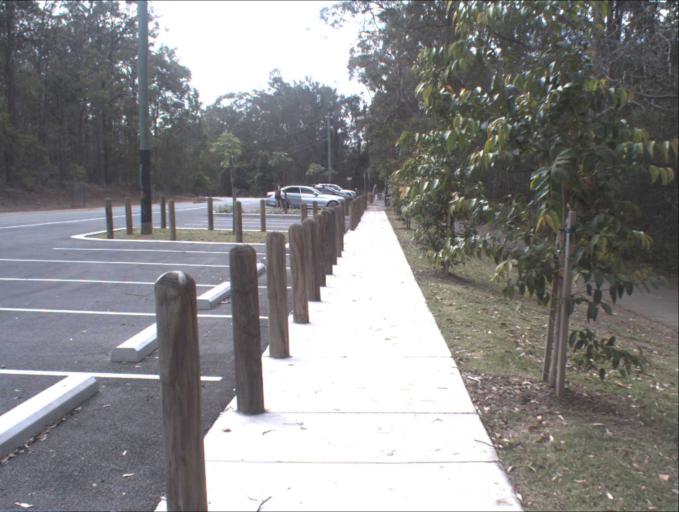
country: AU
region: Queensland
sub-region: Logan
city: Springwood
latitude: -27.6031
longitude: 153.1487
